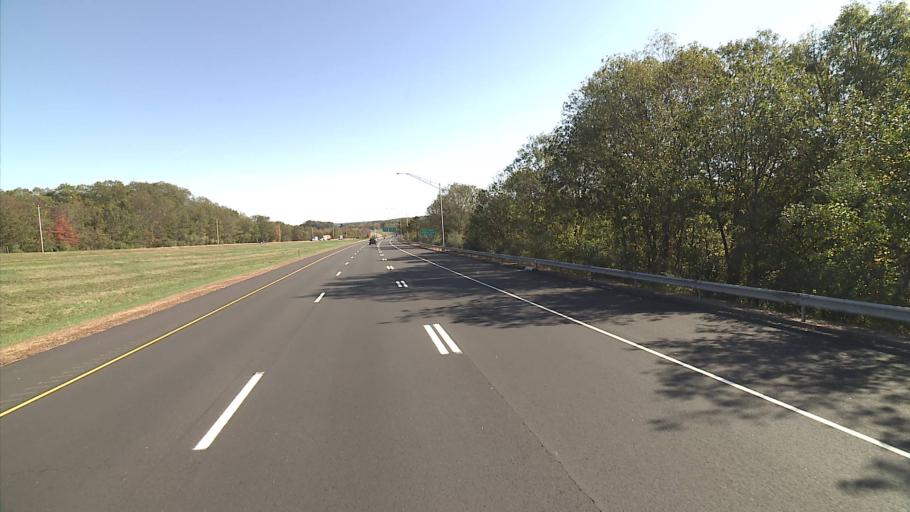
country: US
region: Connecticut
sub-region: Tolland County
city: Mansfield City
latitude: 41.7227
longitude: -72.2608
